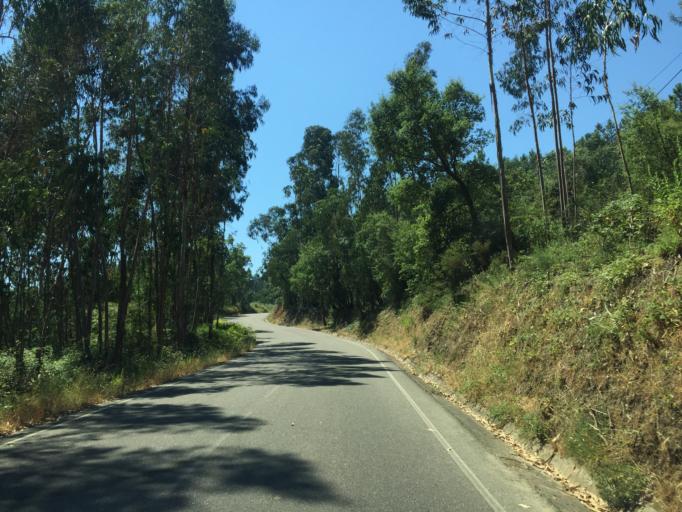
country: PT
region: Santarem
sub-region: Ferreira do Zezere
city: Ferreira do Zezere
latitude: 39.6118
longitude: -8.3119
